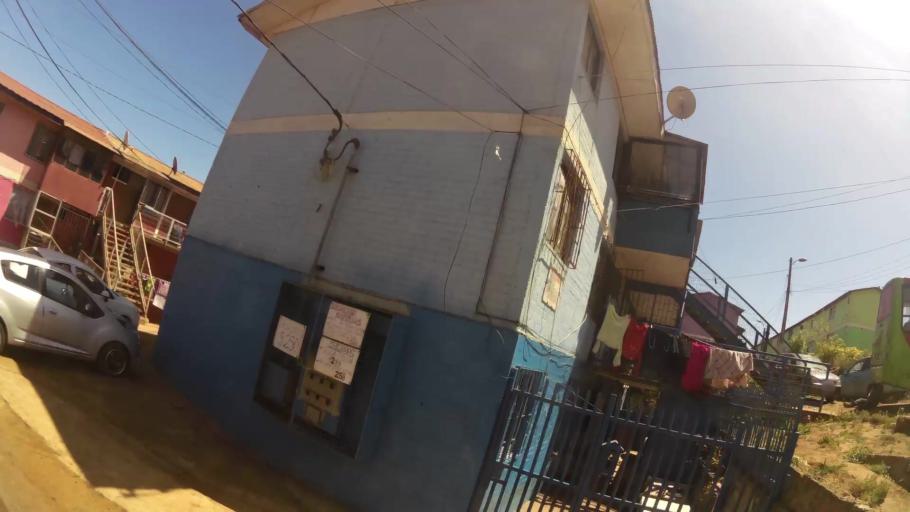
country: CL
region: Valparaiso
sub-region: Provincia de Valparaiso
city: Valparaiso
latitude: -33.0363
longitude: -71.6546
